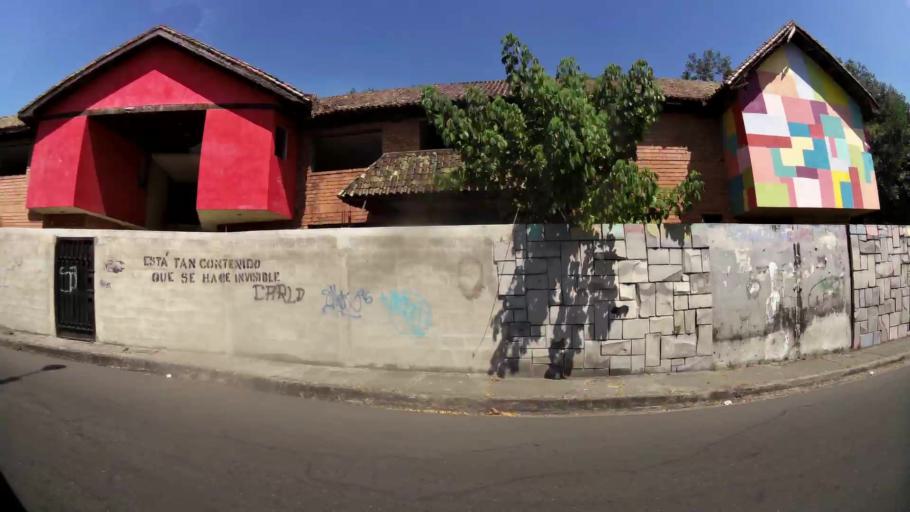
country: EC
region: Guayas
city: Guayaquil
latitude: -2.1665
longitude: -79.9152
